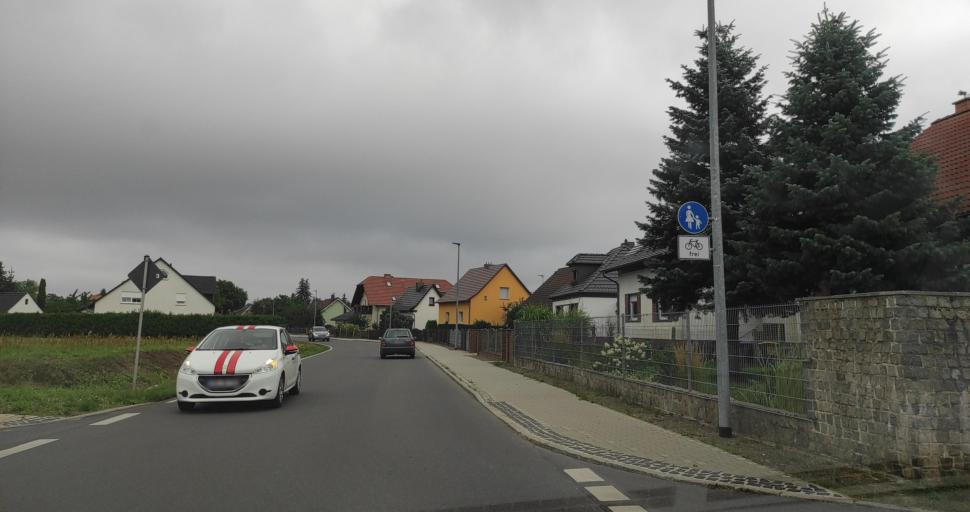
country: DE
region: Brandenburg
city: Forst
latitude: 51.7199
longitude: 14.6356
